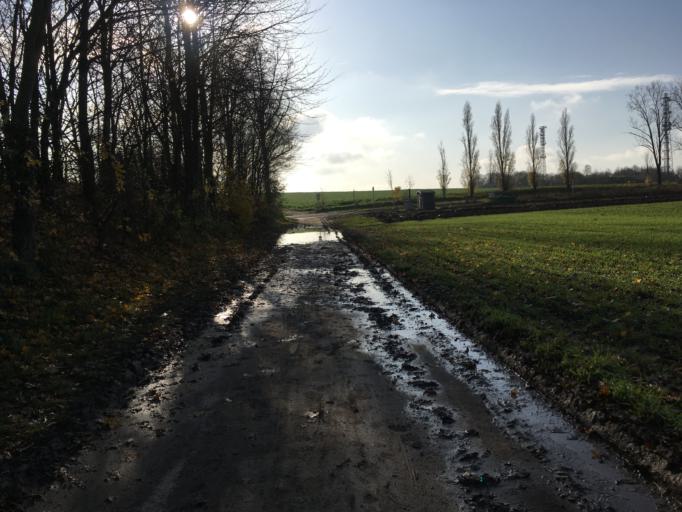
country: DE
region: Rheinland-Pfalz
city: Mainz
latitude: 49.9662
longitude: 8.2943
